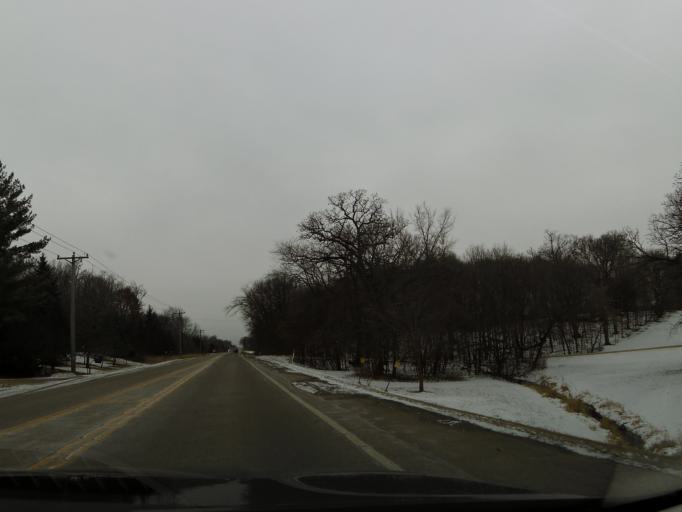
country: US
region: Minnesota
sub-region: Carver County
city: Waconia
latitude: 44.8255
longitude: -93.7884
